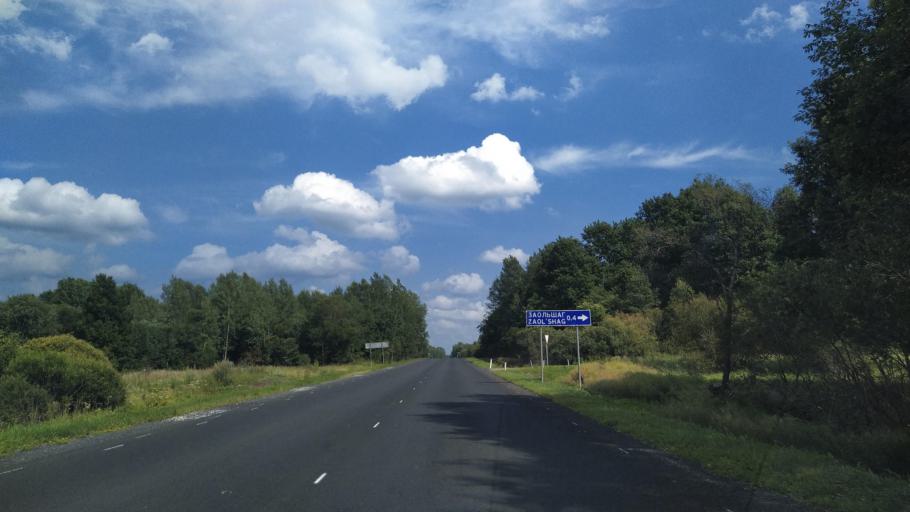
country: RU
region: Pskov
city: Porkhov
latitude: 57.7275
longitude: 29.3077
